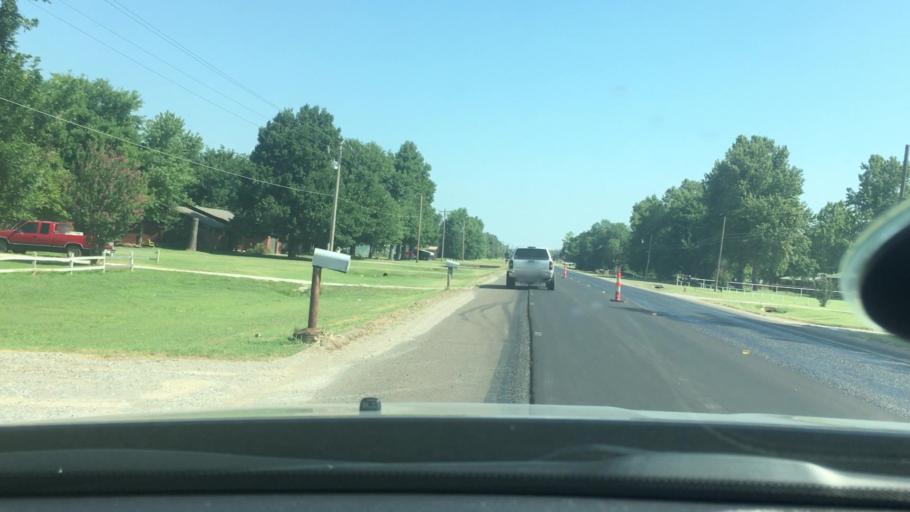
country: US
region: Oklahoma
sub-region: Garvin County
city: Lindsay
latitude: 34.8059
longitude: -97.5983
